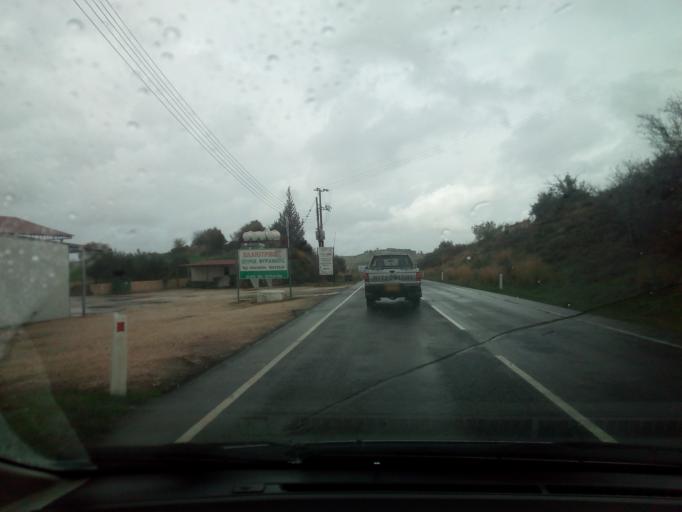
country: CY
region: Pafos
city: Polis
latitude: 35.0006
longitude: 32.4447
